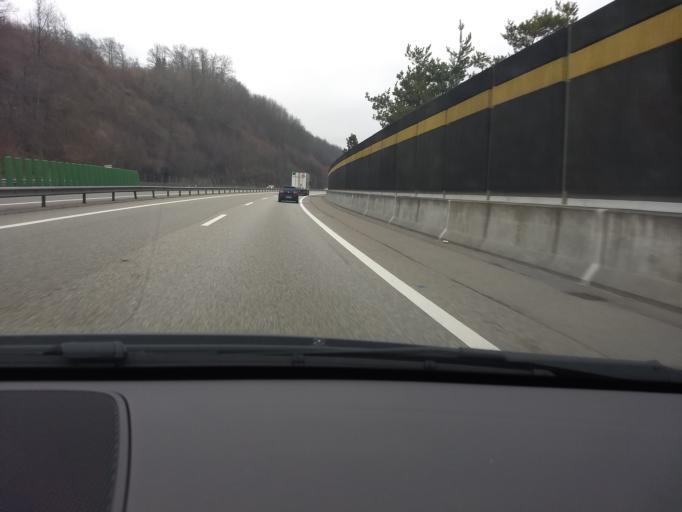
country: CH
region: Basel-Landschaft
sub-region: Bezirk Waldenburg
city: Diegten
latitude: 47.4171
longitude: 7.8083
